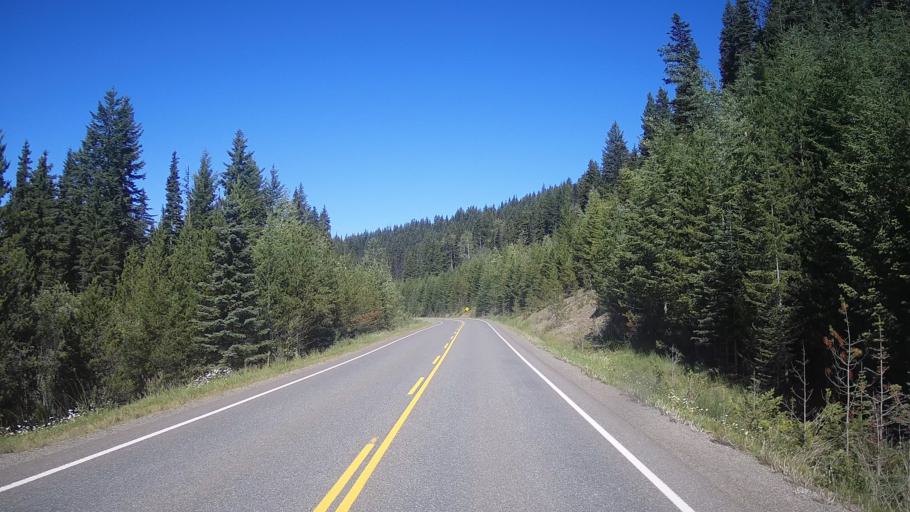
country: CA
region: British Columbia
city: Kamloops
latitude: 51.4985
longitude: -120.4374
